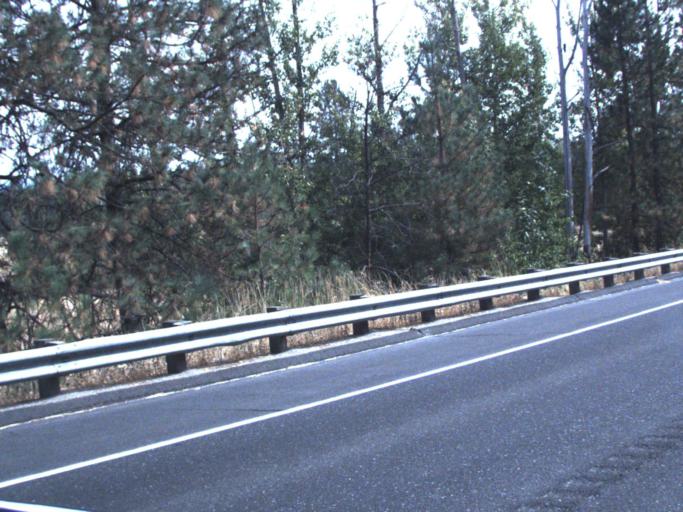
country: US
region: Washington
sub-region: Spokane County
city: Deer Park
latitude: 47.9248
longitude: -117.4602
